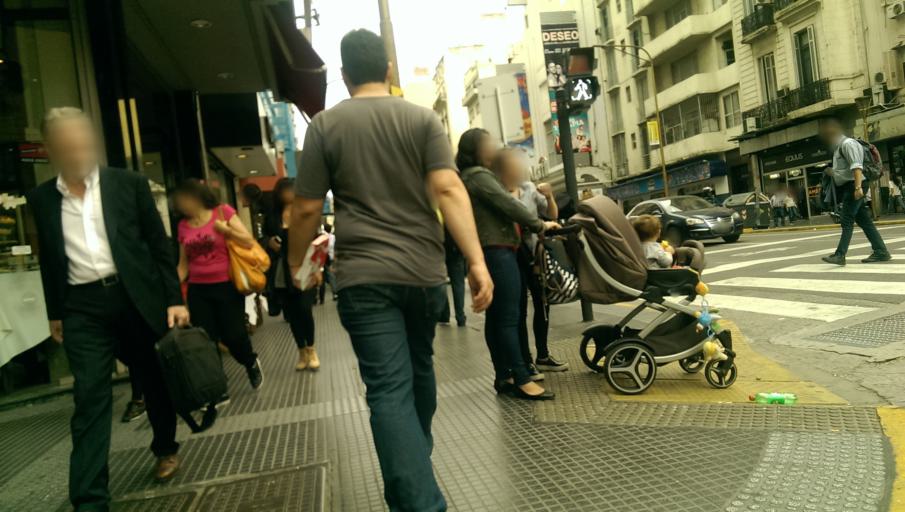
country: AR
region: Buenos Aires F.D.
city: Buenos Aires
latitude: -34.6038
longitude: -58.3851
